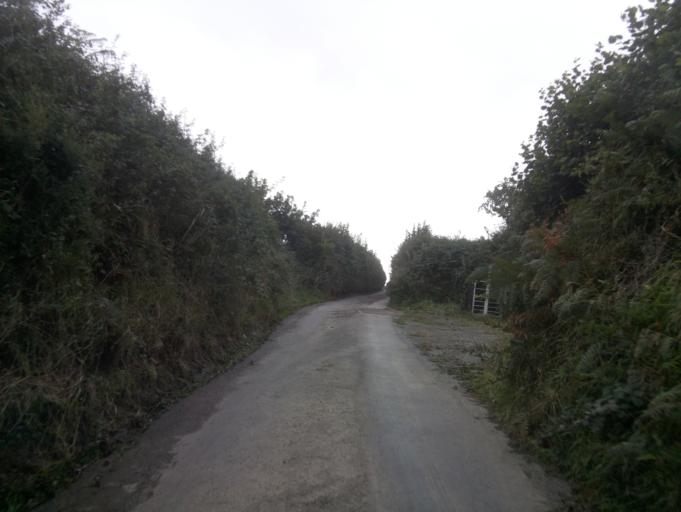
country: GB
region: England
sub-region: Devon
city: Kingsbridge
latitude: 50.2783
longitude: -3.8163
